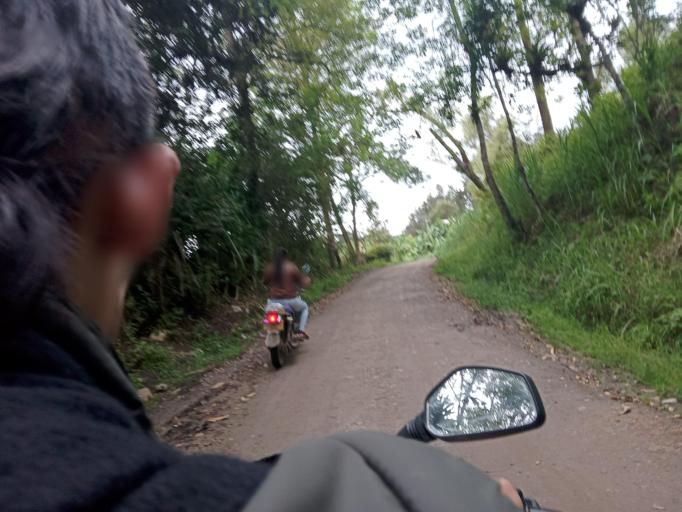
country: CO
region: Cundinamarca
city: Tenza
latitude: 5.1030
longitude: -73.4307
